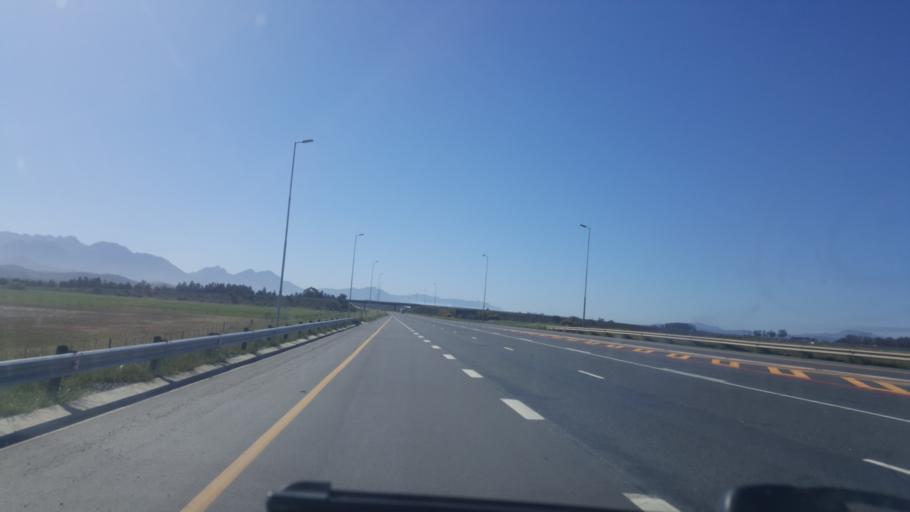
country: ZA
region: Western Cape
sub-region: Cape Winelands District Municipality
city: Worcester
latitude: -33.6347
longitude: 19.3634
